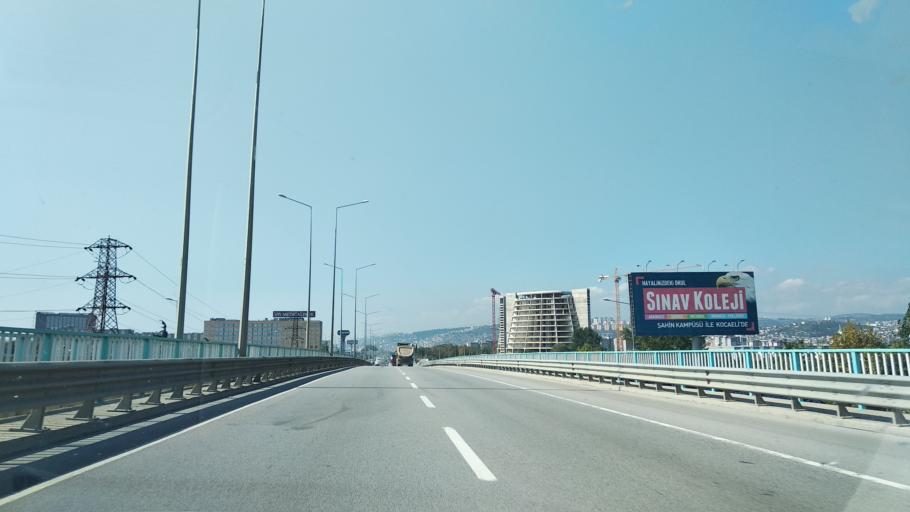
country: TR
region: Kocaeli
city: Kosekoy
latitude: 40.7585
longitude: 29.9883
